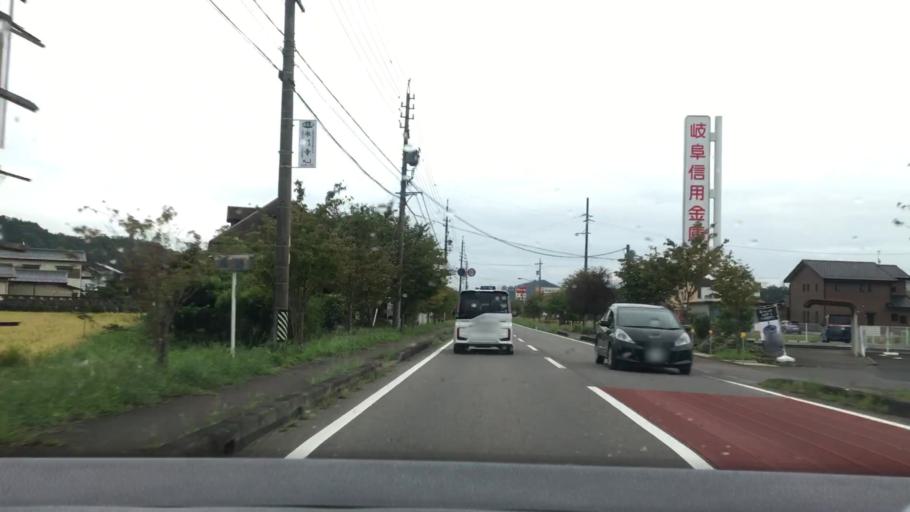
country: JP
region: Gifu
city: Mino
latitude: 35.5231
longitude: 136.8520
